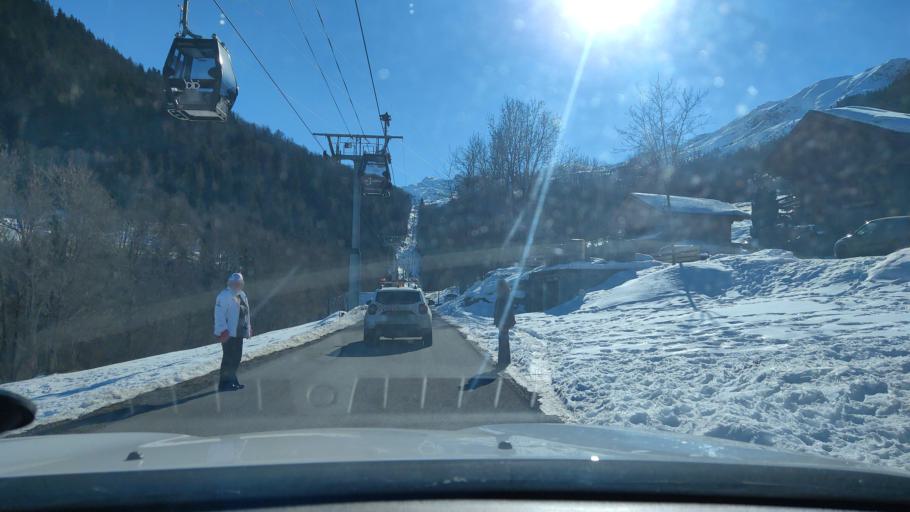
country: FR
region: Rhone-Alpes
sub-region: Departement de la Savoie
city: Les Allues
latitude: 45.4266
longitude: 6.5577
